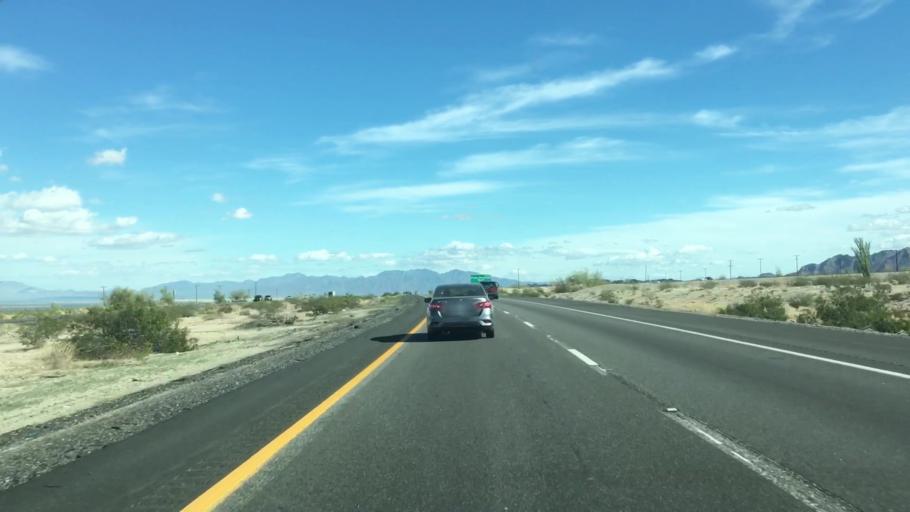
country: US
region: California
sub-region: Imperial County
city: Niland
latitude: 33.7005
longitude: -115.4590
